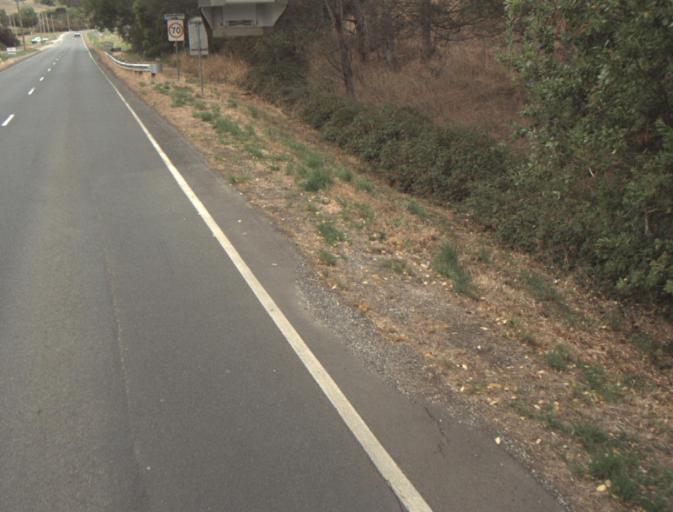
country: AU
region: Tasmania
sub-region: Launceston
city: Mayfield
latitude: -41.2552
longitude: 147.2161
